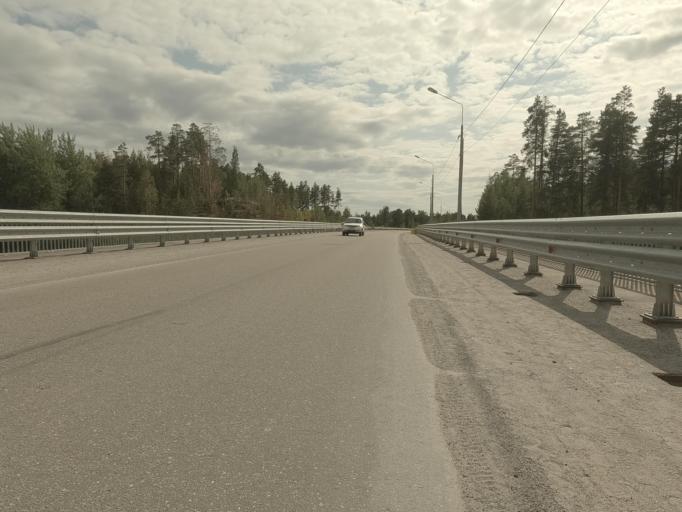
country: RU
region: Leningrad
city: Kamennogorsk
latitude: 60.9593
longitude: 29.1390
